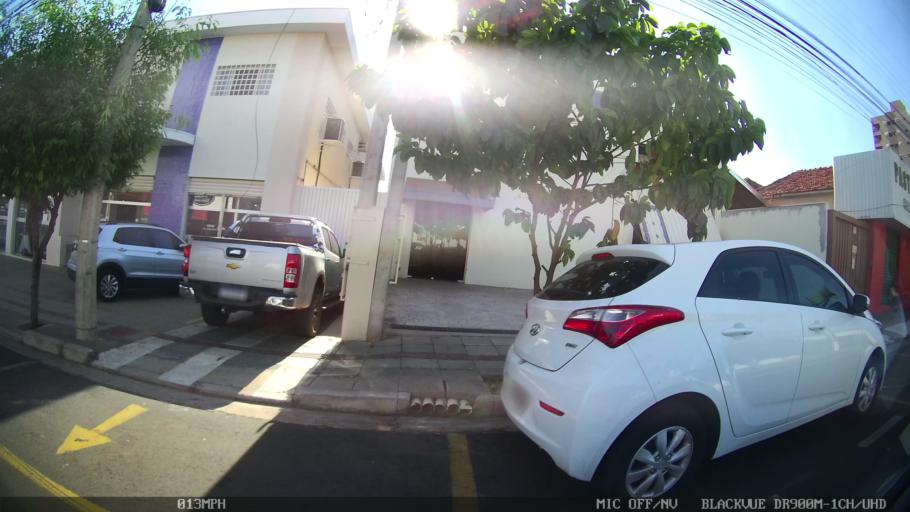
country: BR
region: Sao Paulo
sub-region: Sao Jose Do Rio Preto
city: Sao Jose do Rio Preto
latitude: -20.8040
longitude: -49.3731
